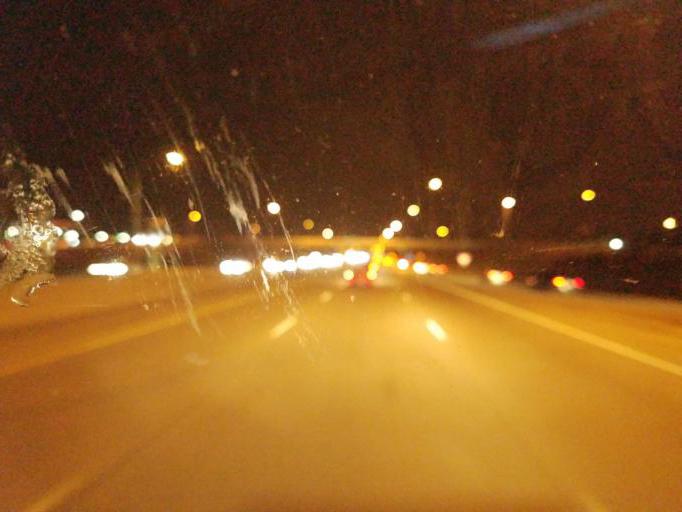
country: US
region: Iowa
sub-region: Polk County
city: Clive
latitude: 41.5922
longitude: -93.7541
